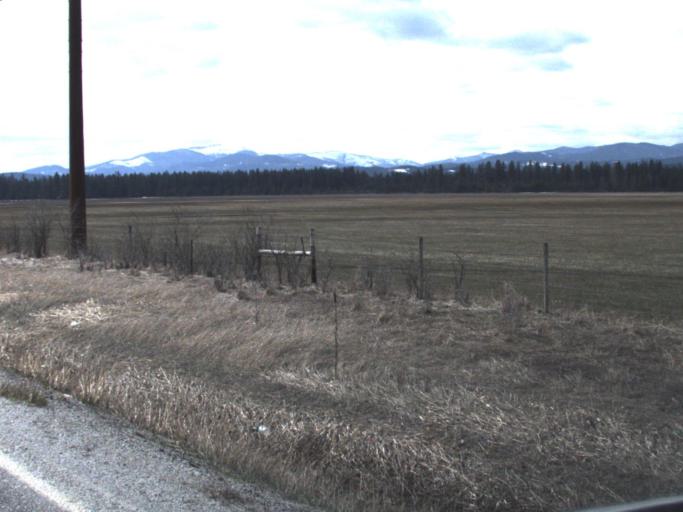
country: US
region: Washington
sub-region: Pend Oreille County
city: Newport
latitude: 48.3548
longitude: -117.3046
